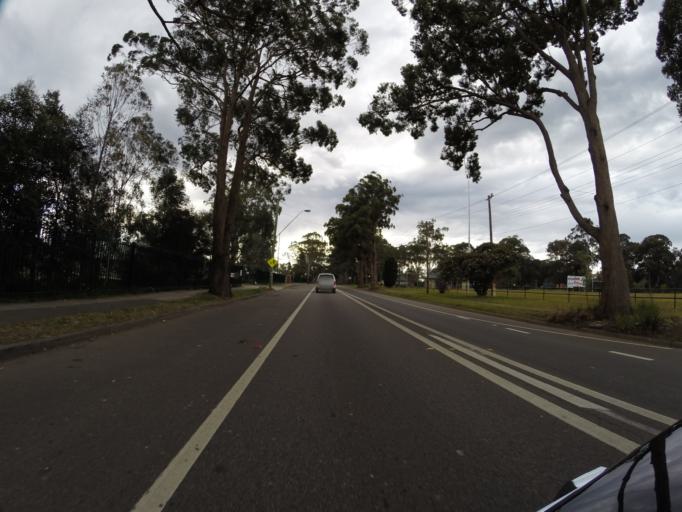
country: AU
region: New South Wales
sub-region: Wollondilly
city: Douglas Park
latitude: -34.1990
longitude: 150.7882
